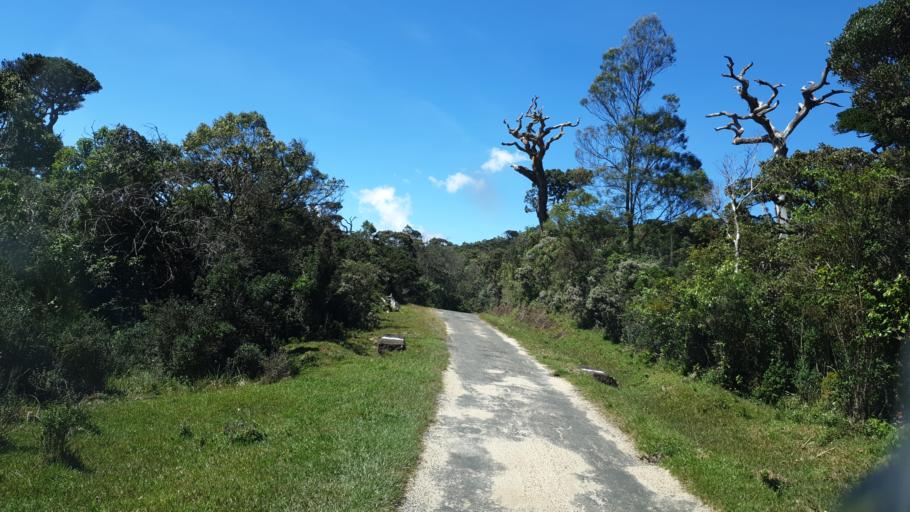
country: LK
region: Uva
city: Haputale
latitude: 6.7995
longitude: 80.8335
